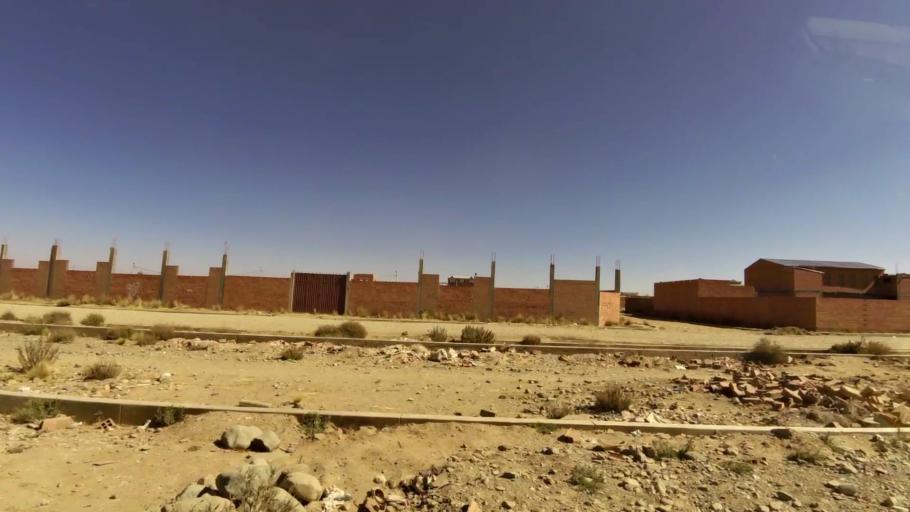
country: BO
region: La Paz
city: La Paz
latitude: -16.5967
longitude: -68.1989
